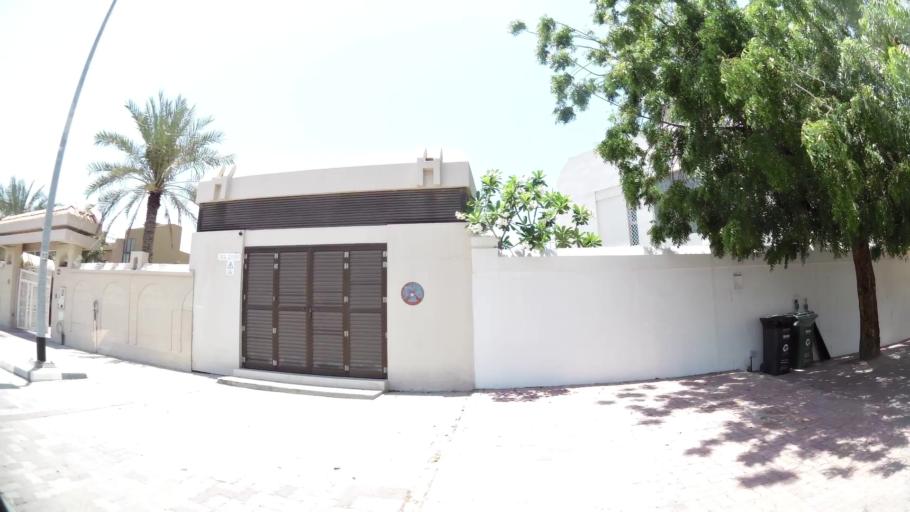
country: AE
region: Dubai
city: Dubai
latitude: 25.2118
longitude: 55.2496
